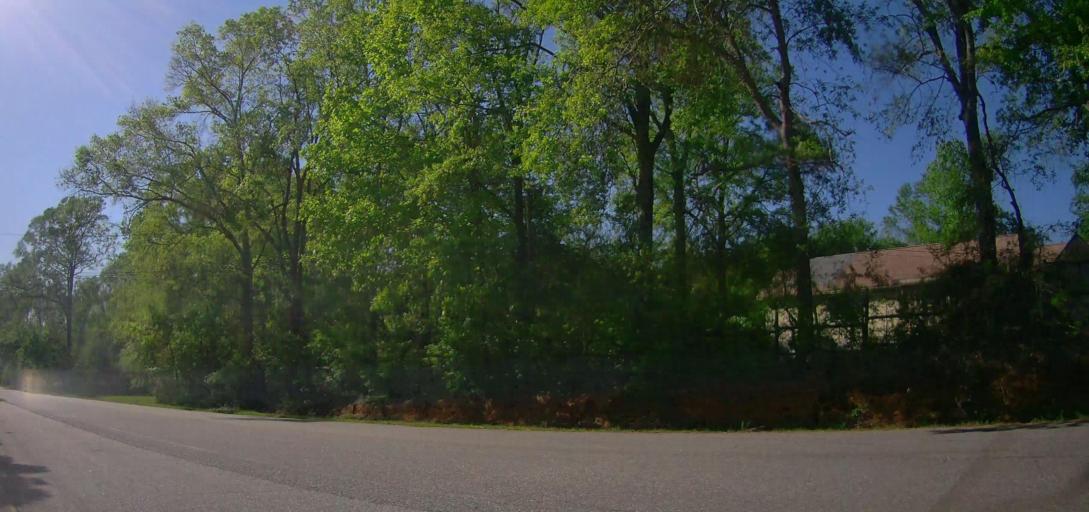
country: US
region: Georgia
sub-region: Houston County
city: Robins Air Force Base
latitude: 32.5437
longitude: -83.5912
